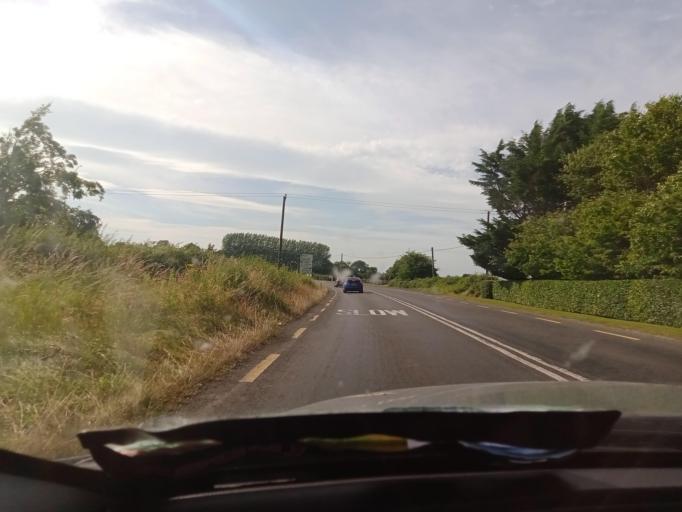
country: IE
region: Leinster
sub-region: Laois
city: Mountmellick
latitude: 53.1239
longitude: -7.3746
